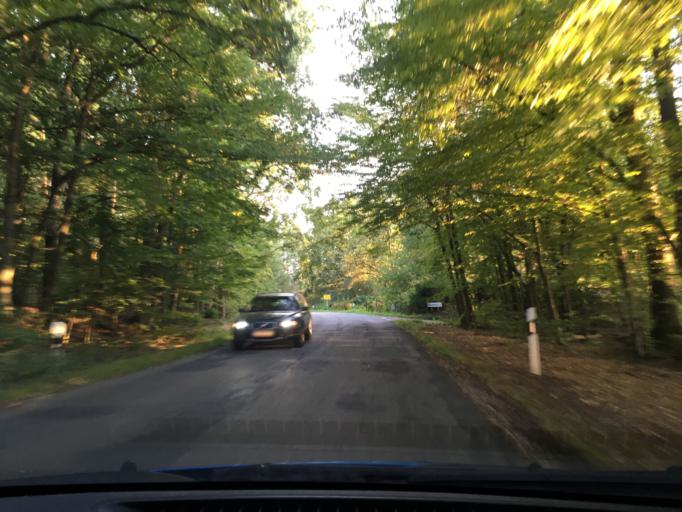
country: DE
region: Lower Saxony
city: Bleckede
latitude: 53.2672
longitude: 10.7023
